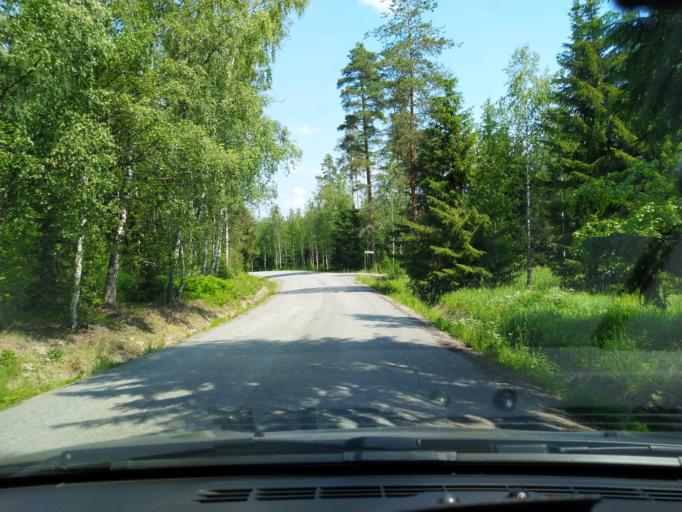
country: FI
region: Uusimaa
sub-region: Helsinki
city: Saukkola
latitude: 60.3645
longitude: 24.1029
